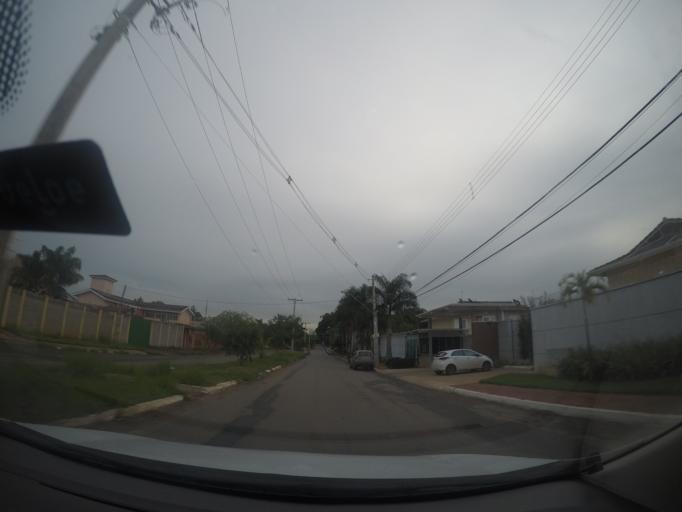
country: BR
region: Goias
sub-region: Goiania
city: Goiania
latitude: -16.6368
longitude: -49.2440
